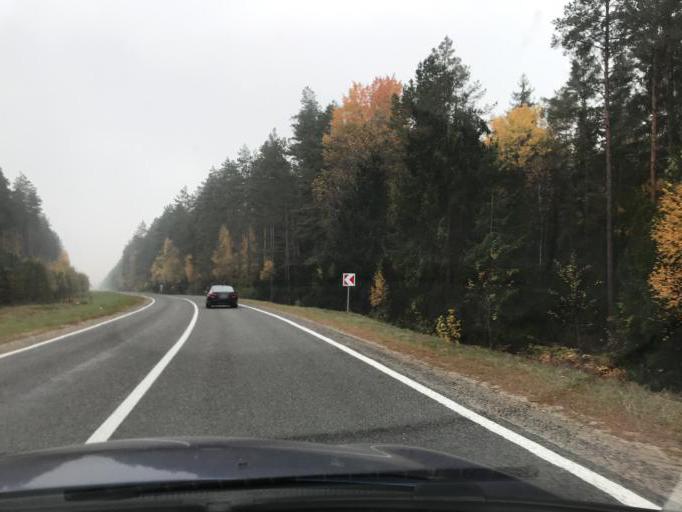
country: LT
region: Alytaus apskritis
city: Druskininkai
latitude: 53.8709
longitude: 23.8951
